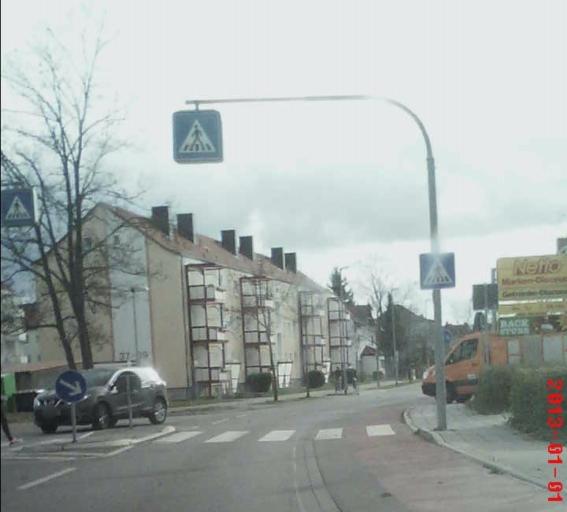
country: DE
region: Thuringia
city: Muehlhausen
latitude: 51.2176
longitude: 10.4446
